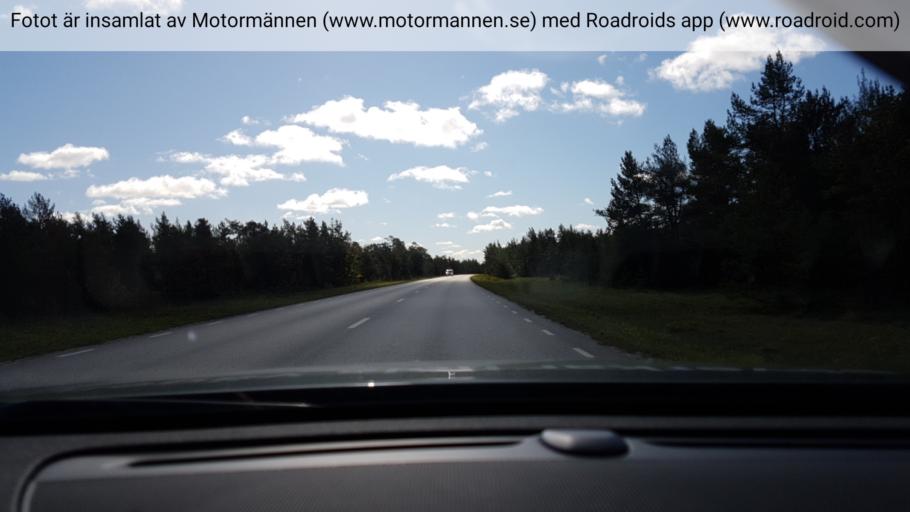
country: SE
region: Gotland
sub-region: Gotland
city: Slite
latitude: 57.7363
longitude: 18.7909
